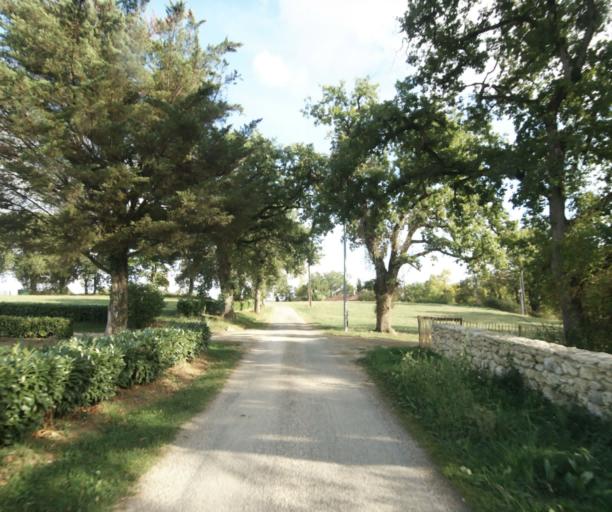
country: FR
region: Midi-Pyrenees
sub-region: Departement du Gers
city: Gondrin
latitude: 43.8937
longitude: 0.2714
